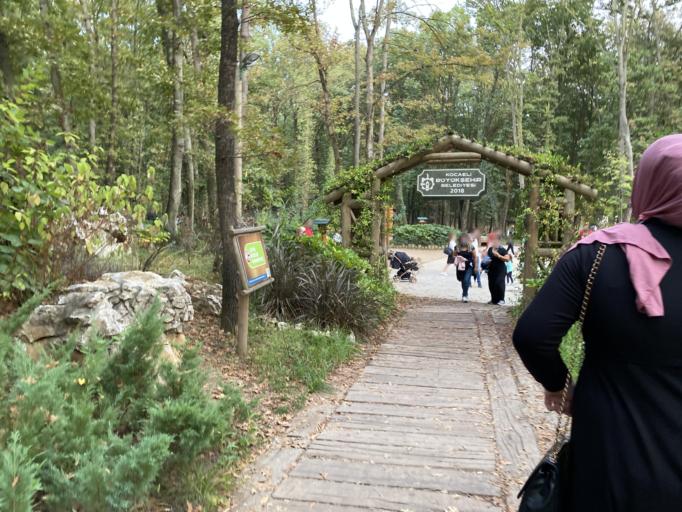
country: TR
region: Kocaeli
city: Derbent
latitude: 40.7334
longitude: 30.1628
